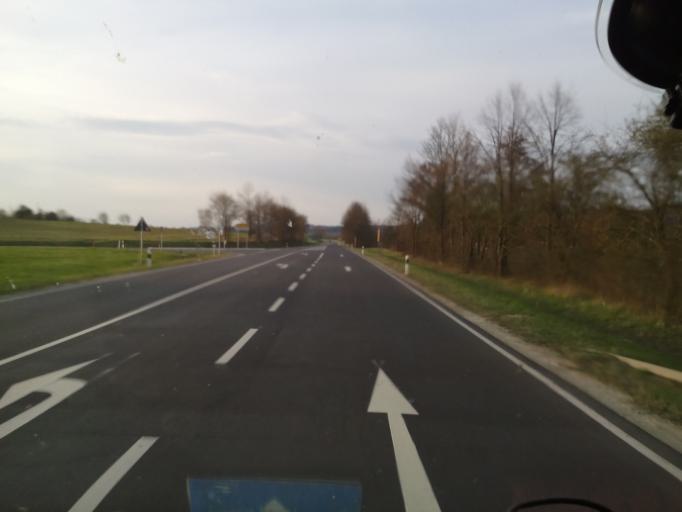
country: DE
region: Bavaria
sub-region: Regierungsbezirk Unterfranken
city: Pfarrweisach
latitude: 50.1249
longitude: 10.7612
